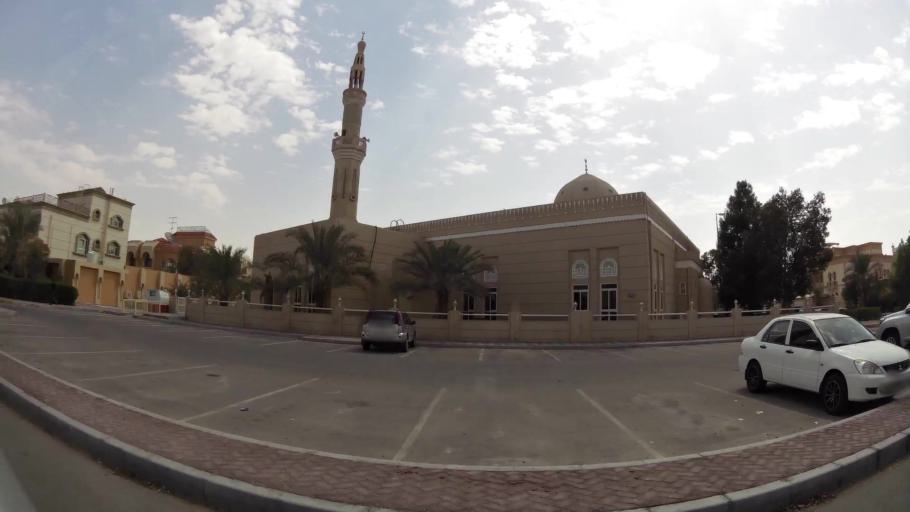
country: AE
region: Abu Dhabi
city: Abu Dhabi
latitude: 24.3120
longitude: 54.6087
